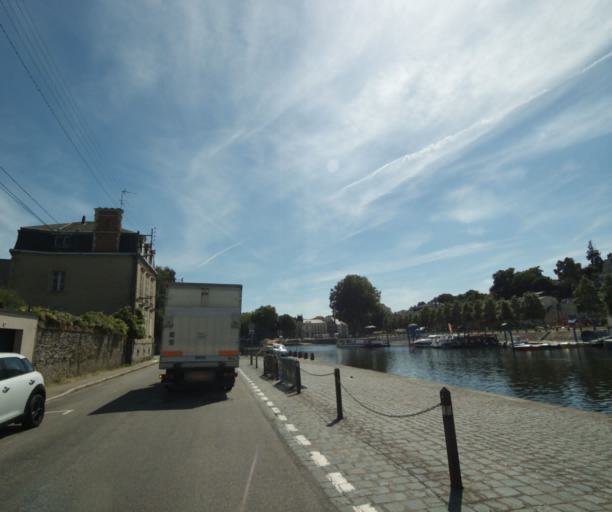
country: FR
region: Pays de la Loire
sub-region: Departement de la Mayenne
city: Laval
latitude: 48.0755
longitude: -0.7701
